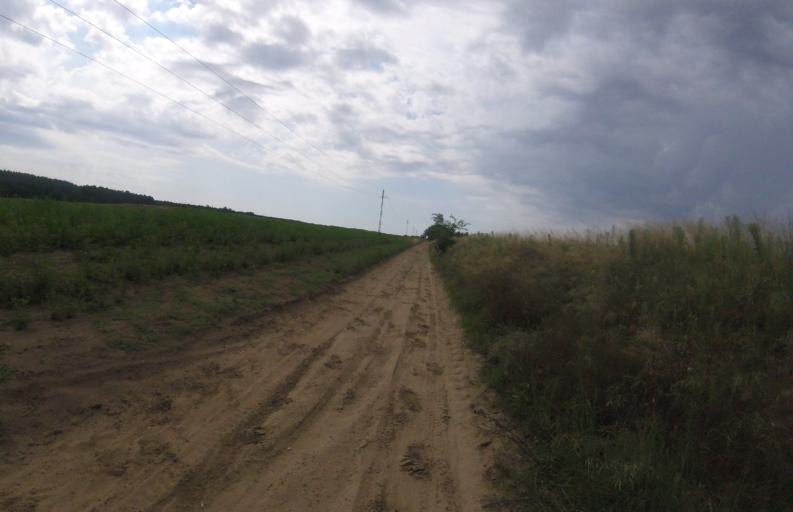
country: HU
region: Pest
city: God
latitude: 47.6680
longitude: 19.1725
